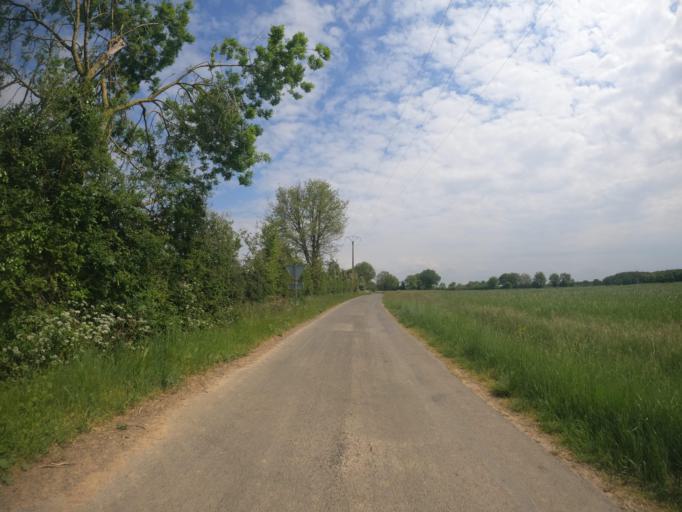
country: FR
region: Poitou-Charentes
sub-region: Departement des Deux-Sevres
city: Saint-Varent
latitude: 46.8926
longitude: -0.2985
